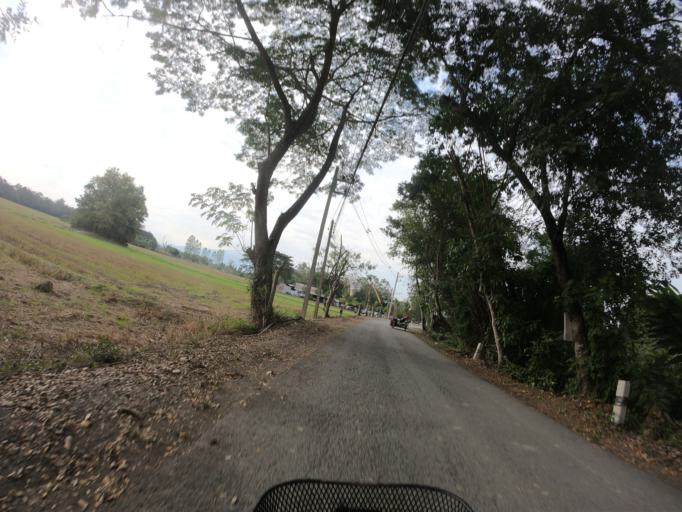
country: TH
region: Chiang Mai
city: San Sai
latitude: 18.7949
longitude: 99.0553
